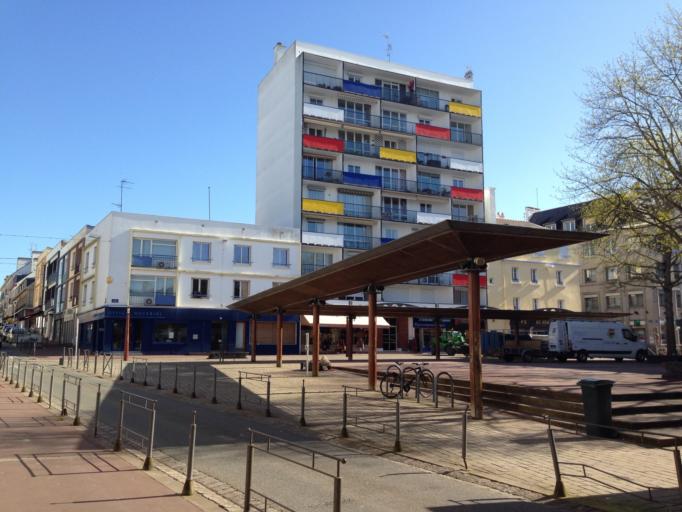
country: FR
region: Brittany
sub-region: Departement du Morbihan
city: Lorient
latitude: 47.7471
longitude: -3.3612
